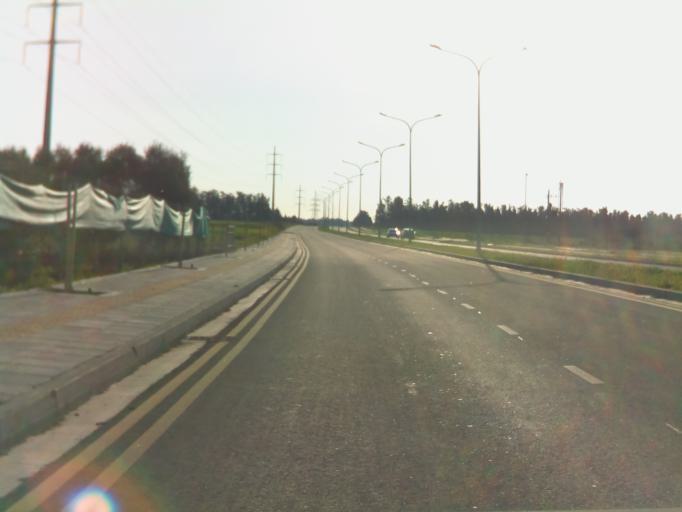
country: CY
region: Pafos
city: Paphos
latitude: 34.7388
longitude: 32.4537
